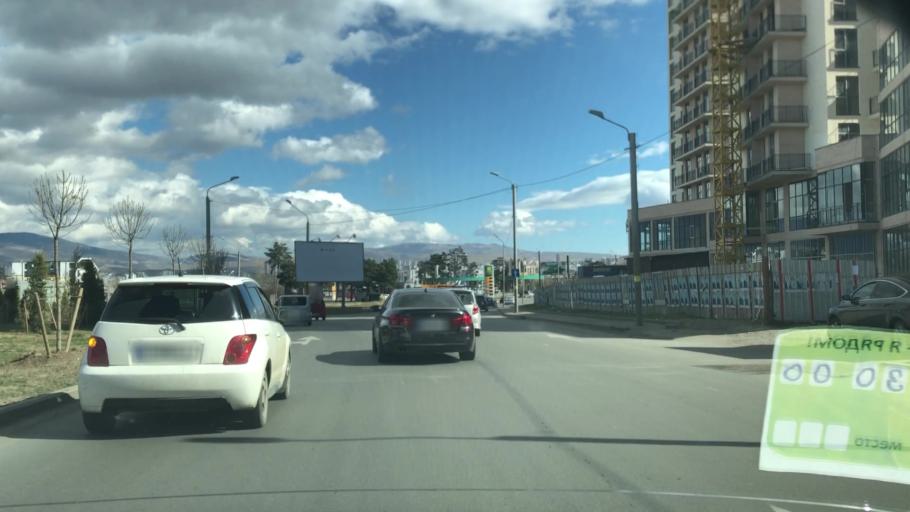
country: GE
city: Zahesi
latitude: 41.7868
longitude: 44.7663
